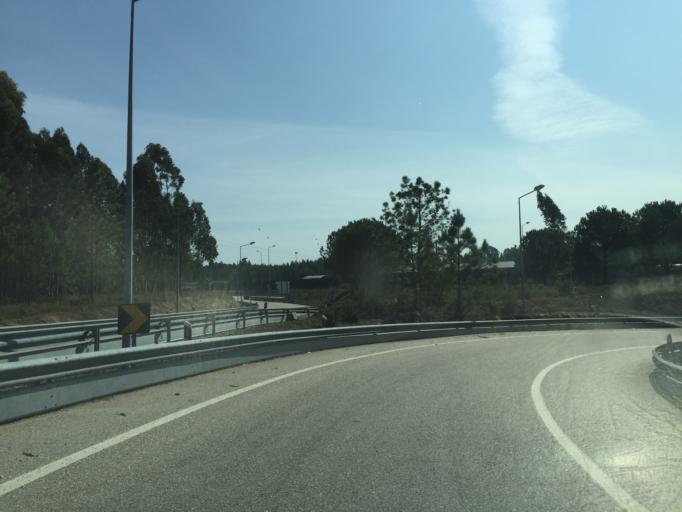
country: PT
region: Leiria
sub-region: Pombal
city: Pombal
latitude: 39.9413
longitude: -8.6717
